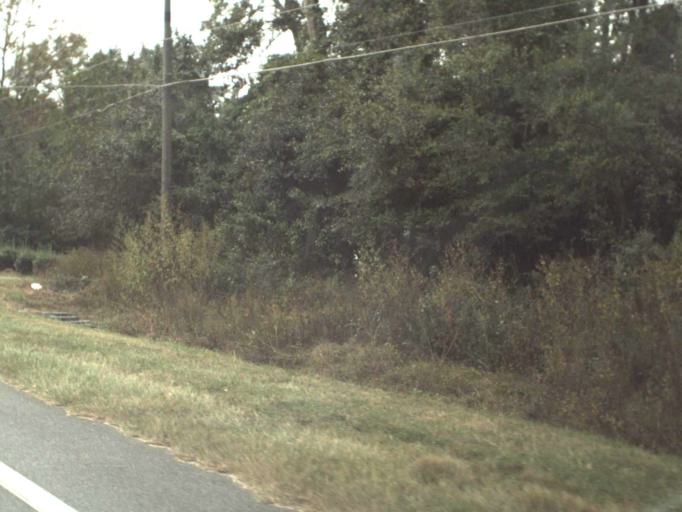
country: US
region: Florida
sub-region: Leon County
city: Tallahassee
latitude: 30.4290
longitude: -84.1941
